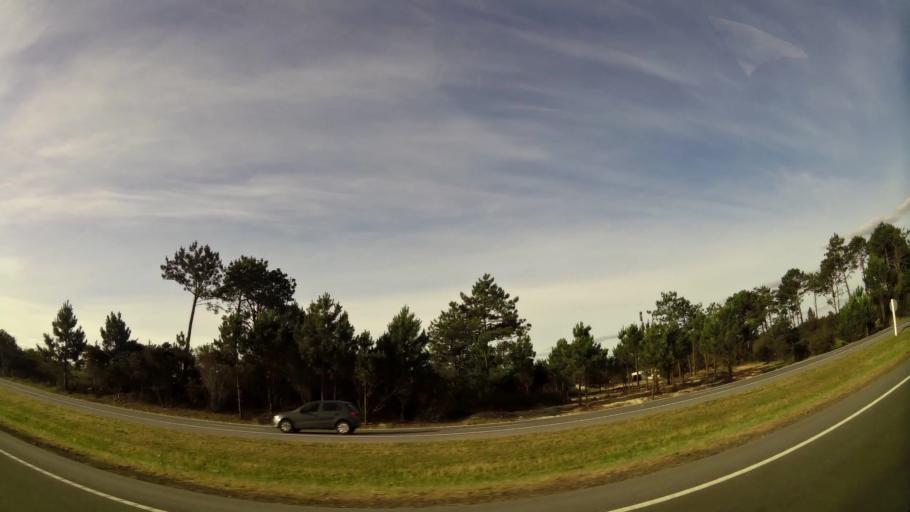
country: UY
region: Maldonado
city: Piriapolis
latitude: -34.7803
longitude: -55.4208
